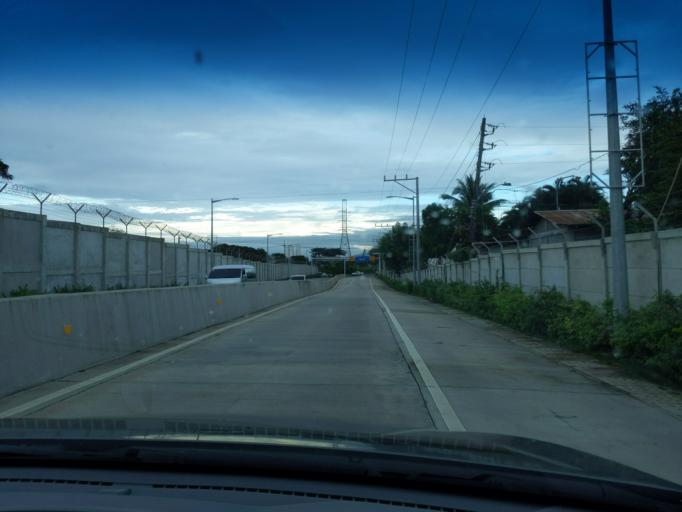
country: PH
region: Calabarzon
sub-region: Province of Cavite
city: Puting Kahoy
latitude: 14.2298
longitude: 121.0485
